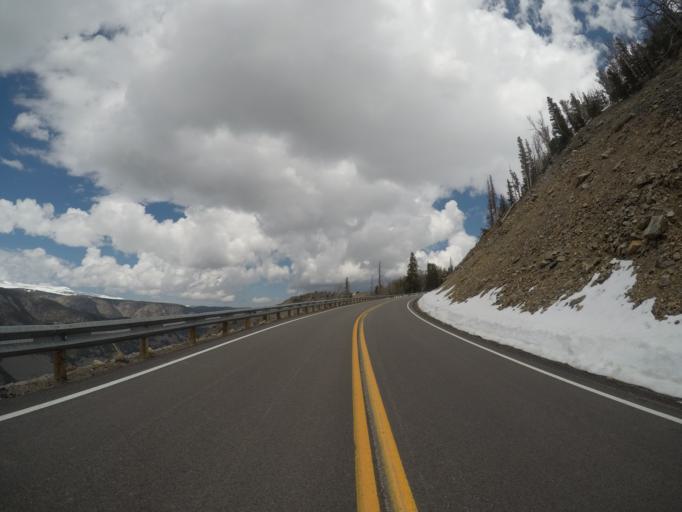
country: US
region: Montana
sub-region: Carbon County
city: Red Lodge
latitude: 45.0390
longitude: -109.4125
